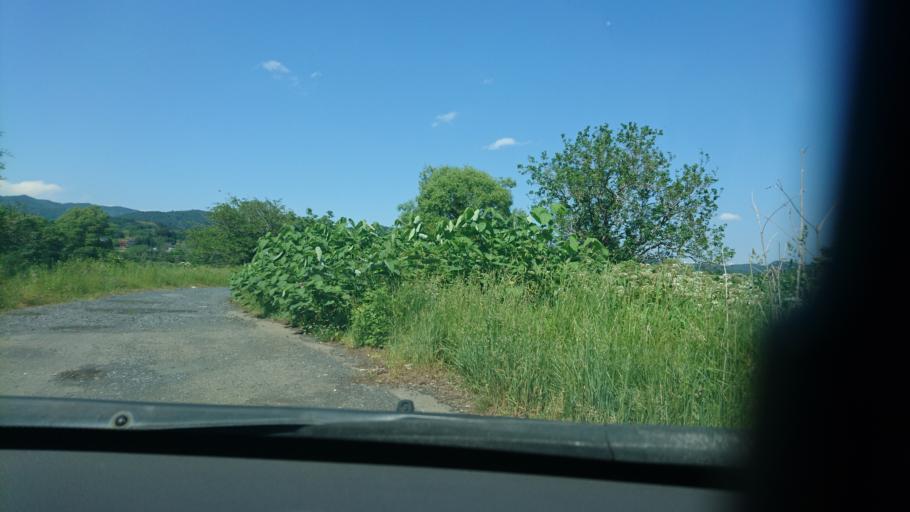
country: JP
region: Iwate
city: Ichinoseki
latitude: 38.9470
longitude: 141.1683
